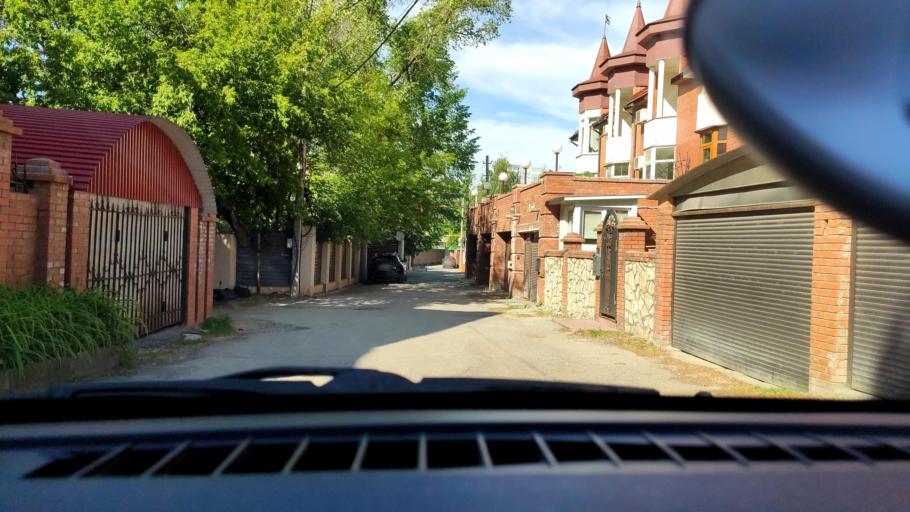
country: RU
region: Samara
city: Samara
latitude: 53.2306
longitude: 50.1745
